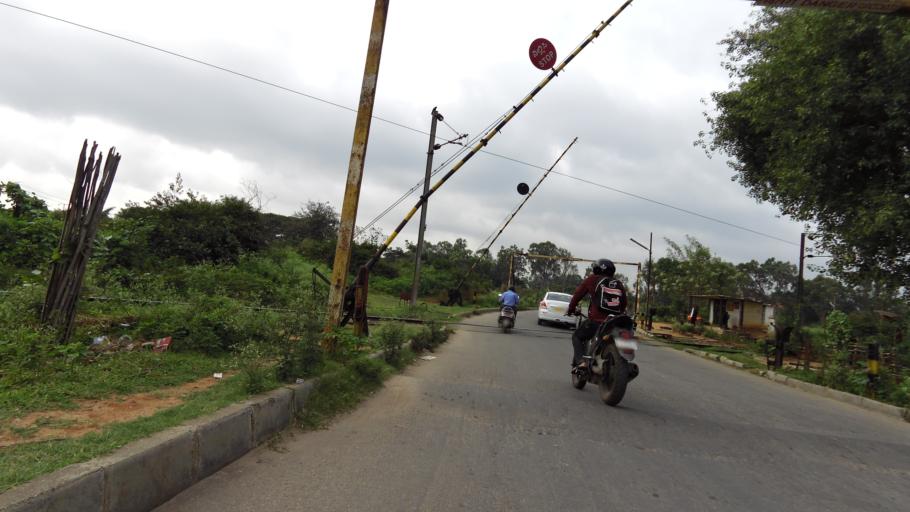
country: IN
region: Karnataka
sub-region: Bangalore Urban
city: Bangalore
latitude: 12.9930
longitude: 77.6451
